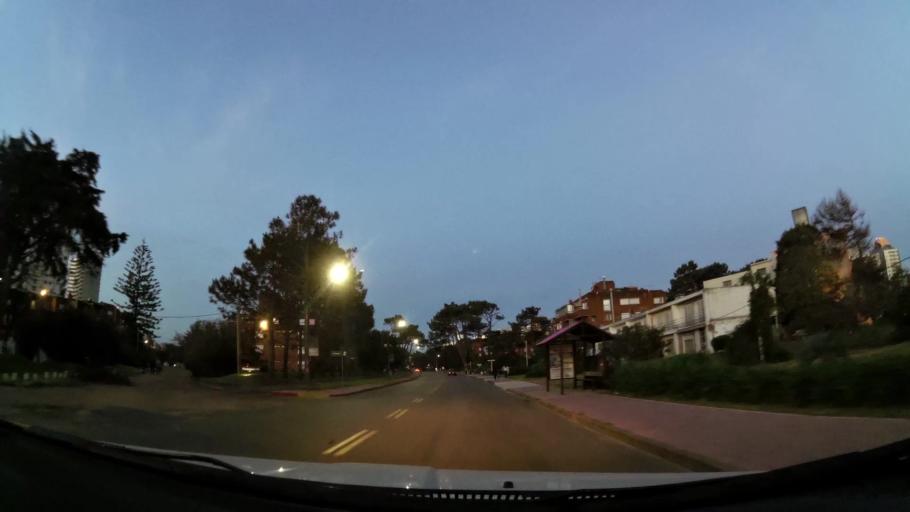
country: UY
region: Maldonado
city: Punta del Este
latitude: -34.9507
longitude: -54.9355
